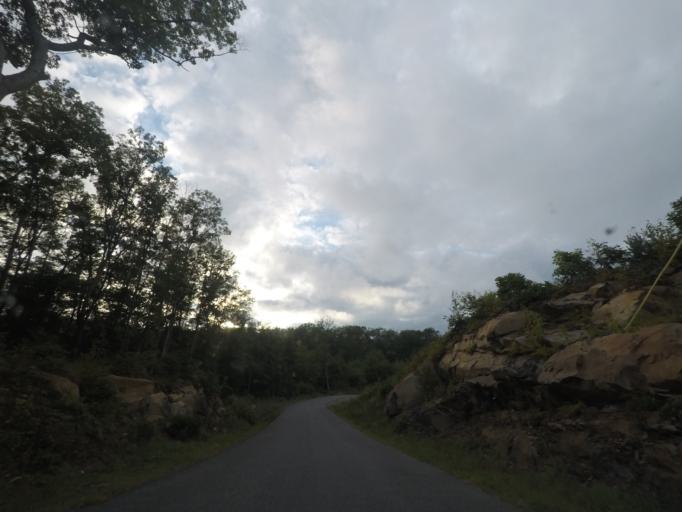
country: US
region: Massachusetts
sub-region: Hampshire County
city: Ware
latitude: 42.2311
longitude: -72.2463
